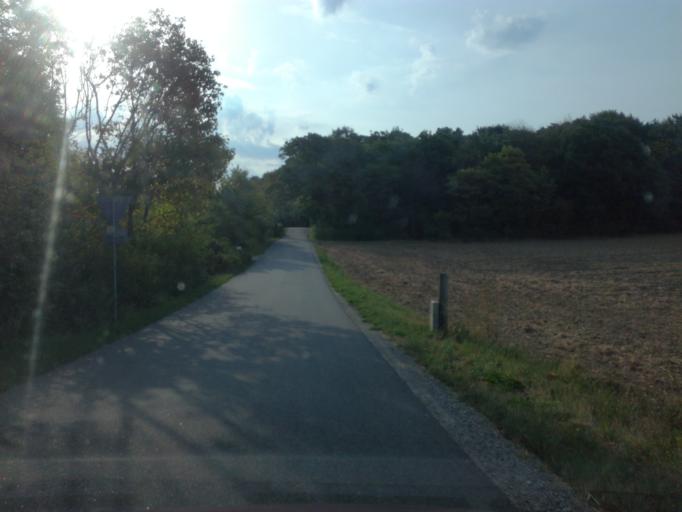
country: DK
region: South Denmark
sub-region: Vejle Kommune
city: Vejle
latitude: 55.6481
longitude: 9.5464
